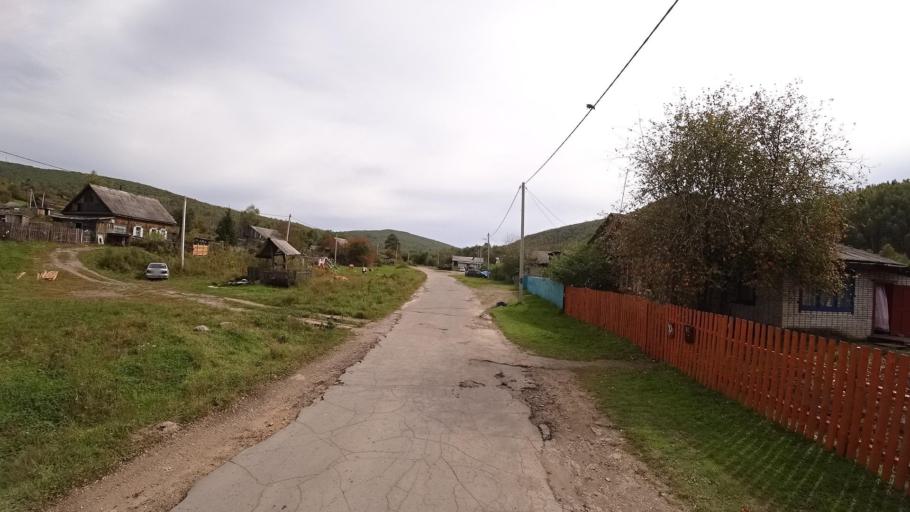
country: RU
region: Jewish Autonomous Oblast
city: Khingansk
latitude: 49.1226
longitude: 131.2049
